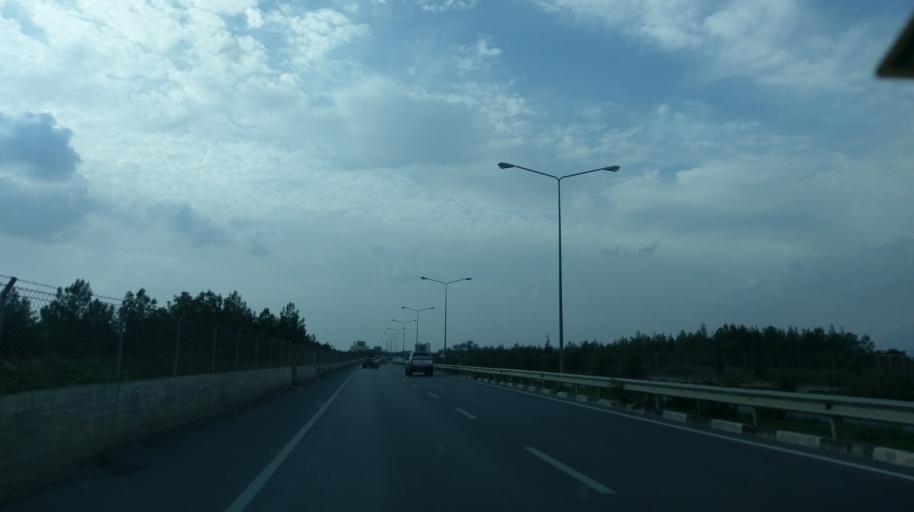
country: CY
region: Lefkosia
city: Nicosia
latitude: 35.1897
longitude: 33.3361
